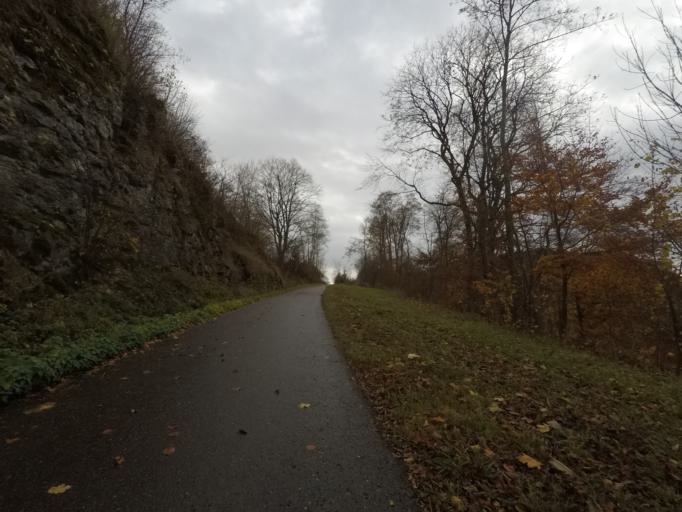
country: DE
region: Baden-Wuerttemberg
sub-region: Tuebingen Region
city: Pfullingen
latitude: 48.4057
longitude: 9.2704
